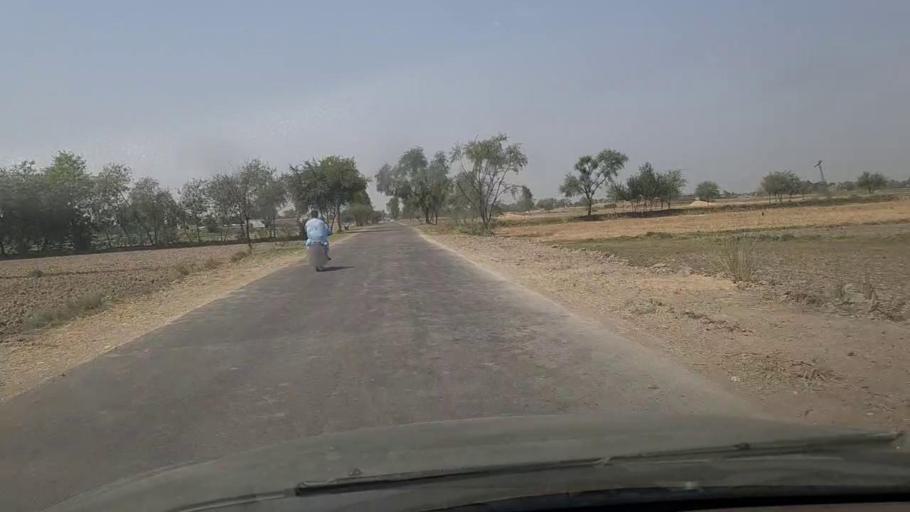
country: PK
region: Sindh
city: Khanpur
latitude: 27.8759
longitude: 69.4592
